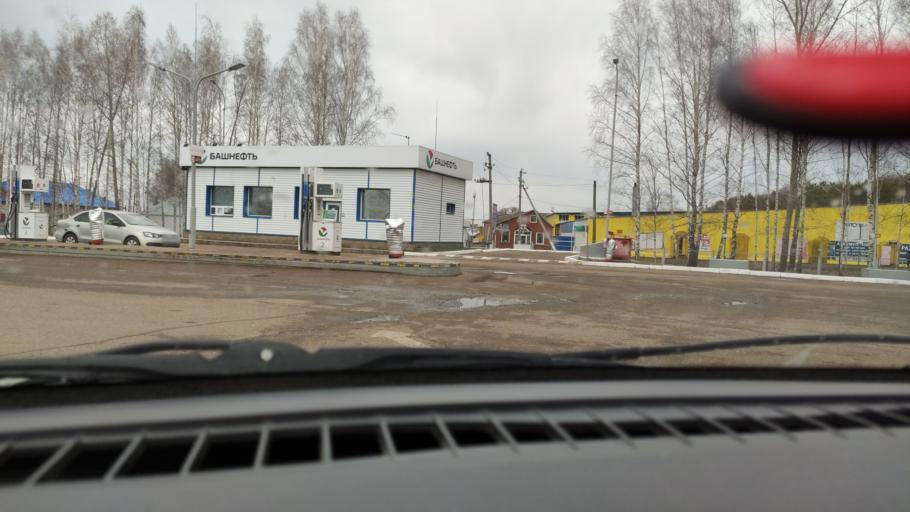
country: RU
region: Bashkortostan
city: Burayevo
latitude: 55.8330
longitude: 55.3978
